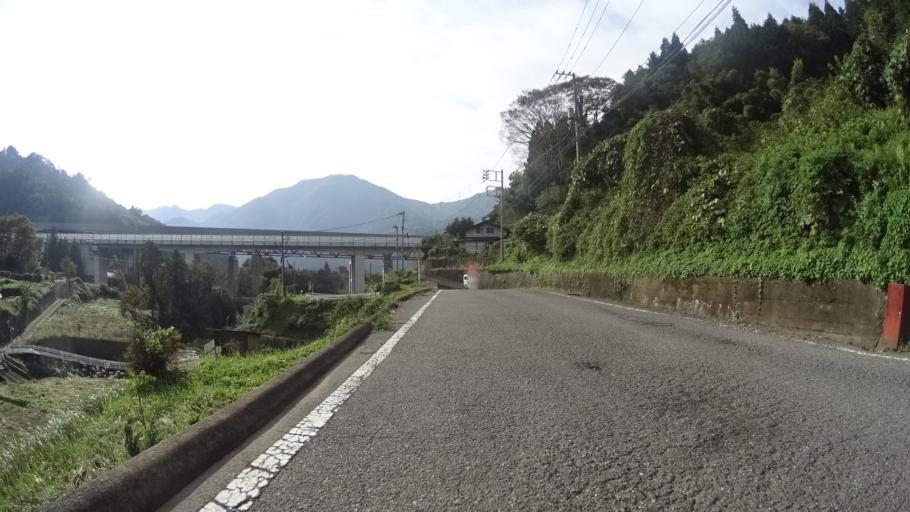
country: JP
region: Yamanashi
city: Otsuki
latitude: 35.6121
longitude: 139.0131
